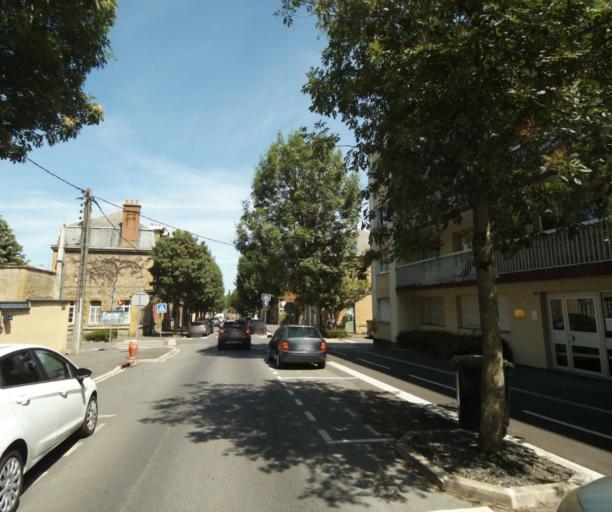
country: FR
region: Champagne-Ardenne
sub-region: Departement des Ardennes
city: Charleville-Mezieres
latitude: 49.7560
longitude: 4.7200
